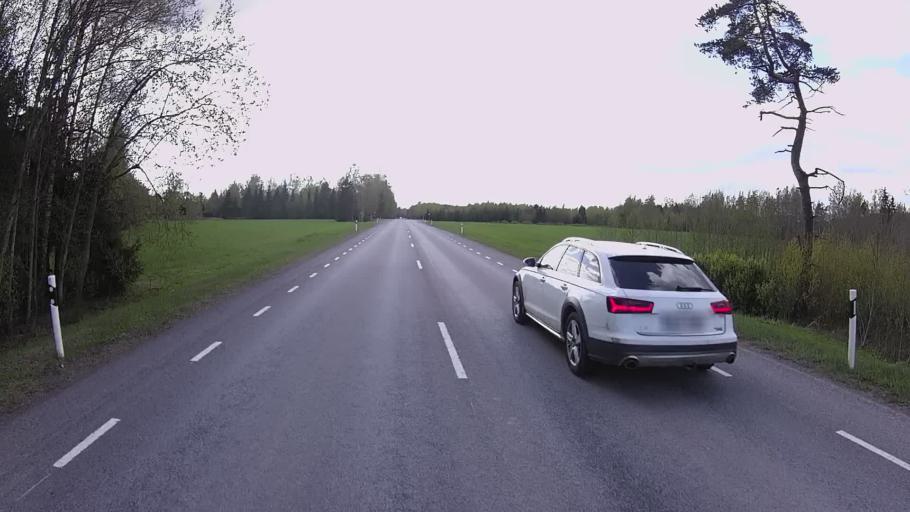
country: EE
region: Tartu
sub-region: Alatskivi vald
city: Kallaste
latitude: 58.5138
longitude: 26.9701
